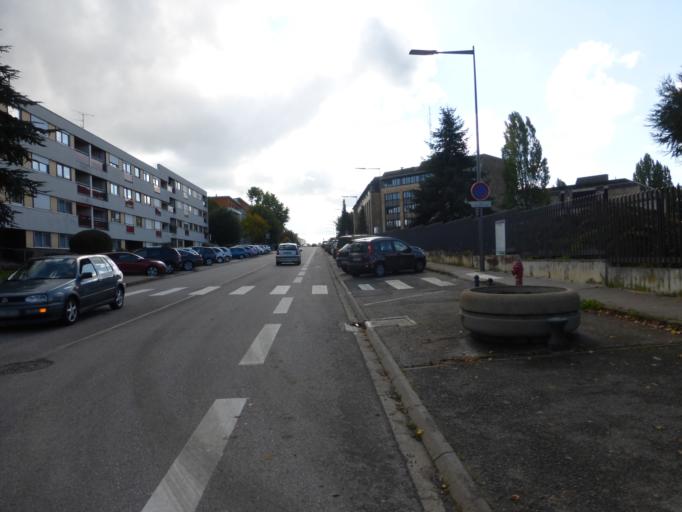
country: FR
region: Lorraine
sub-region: Departement de Meurthe-et-Moselle
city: Villers-les-Nancy
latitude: 48.6763
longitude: 6.1573
